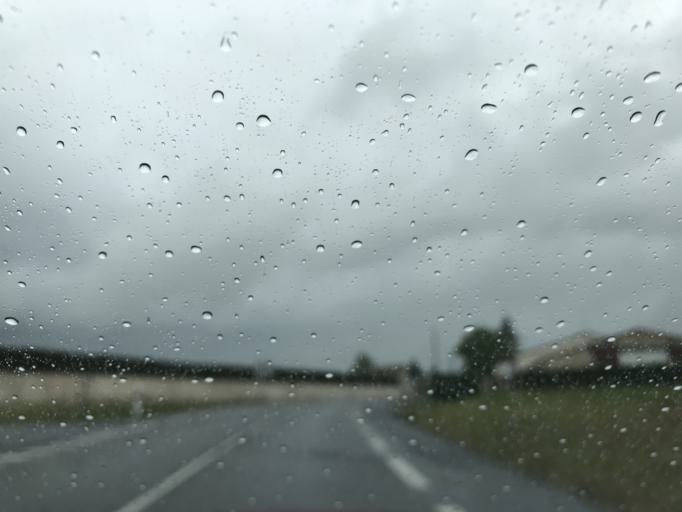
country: FR
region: Auvergne
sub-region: Departement du Puy-de-Dome
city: Montaigut
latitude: 45.6970
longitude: 3.4330
